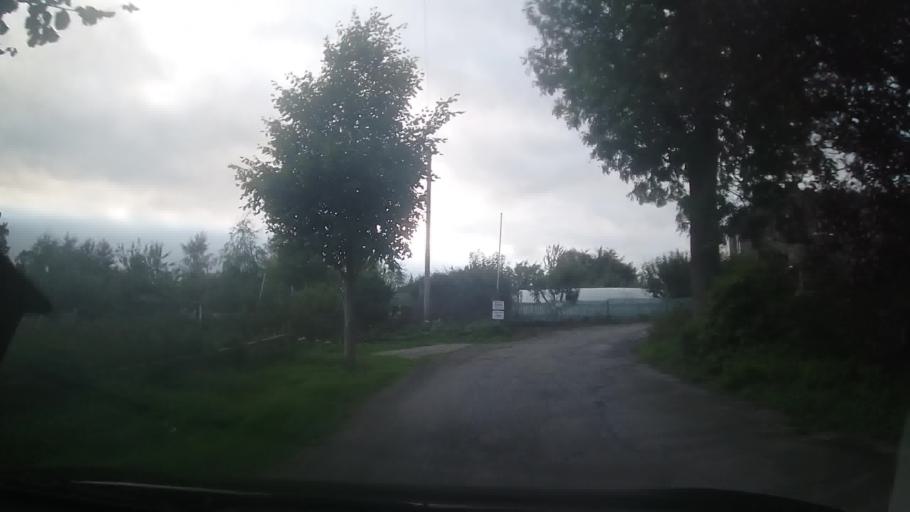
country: GB
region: England
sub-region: Shropshire
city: Bishop's Castle
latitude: 52.5007
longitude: -2.9970
